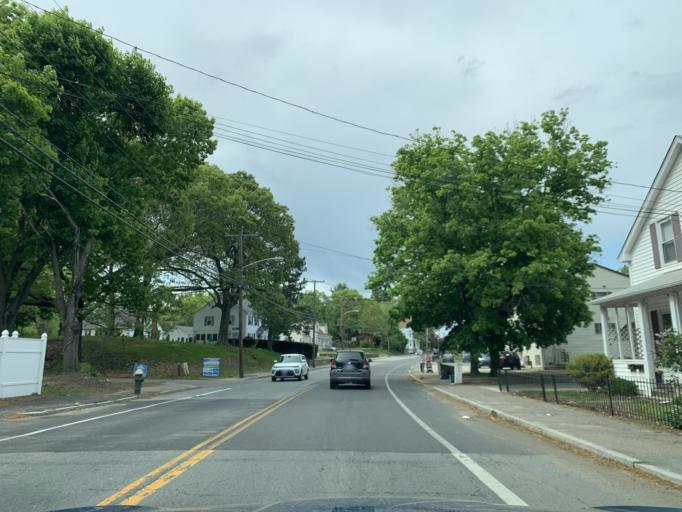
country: US
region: Rhode Island
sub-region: Providence County
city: Johnston
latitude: 41.7984
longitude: -71.4856
